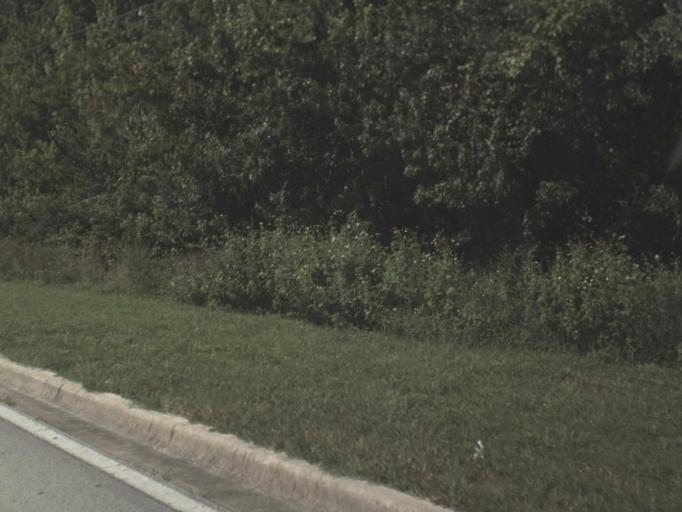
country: US
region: Florida
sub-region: Polk County
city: Jan-Phyl Village
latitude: 28.0085
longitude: -81.7933
